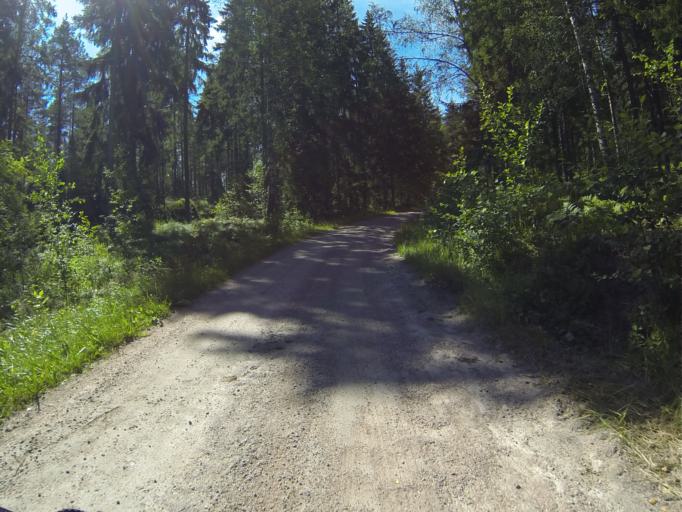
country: FI
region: Varsinais-Suomi
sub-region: Salo
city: Salo
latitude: 60.2926
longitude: 23.0845
